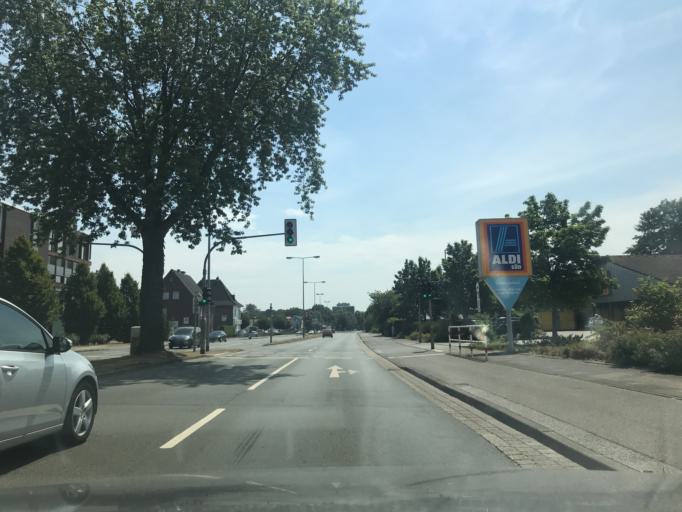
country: DE
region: North Rhine-Westphalia
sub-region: Regierungsbezirk Dusseldorf
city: Wesel
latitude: 51.6752
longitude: 6.6072
